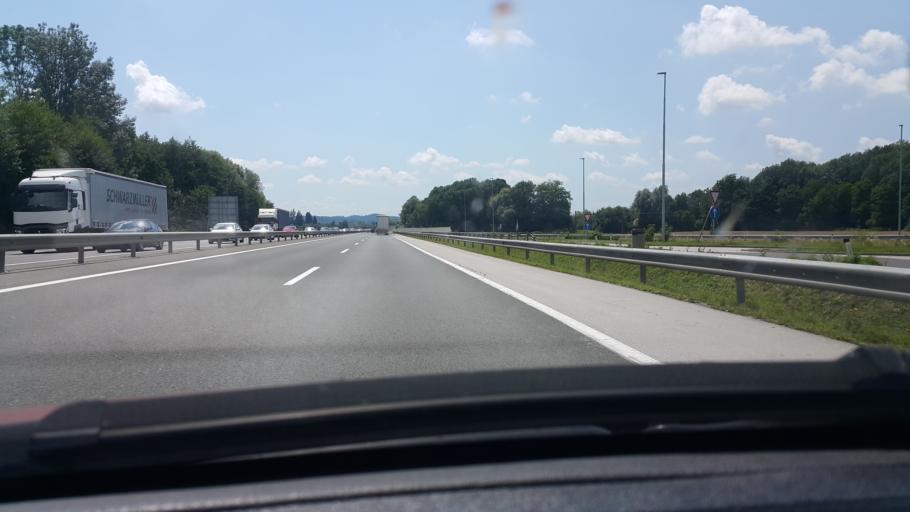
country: SI
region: Lukovica
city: Lukovica pri Domzalah
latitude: 46.1644
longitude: 14.6871
